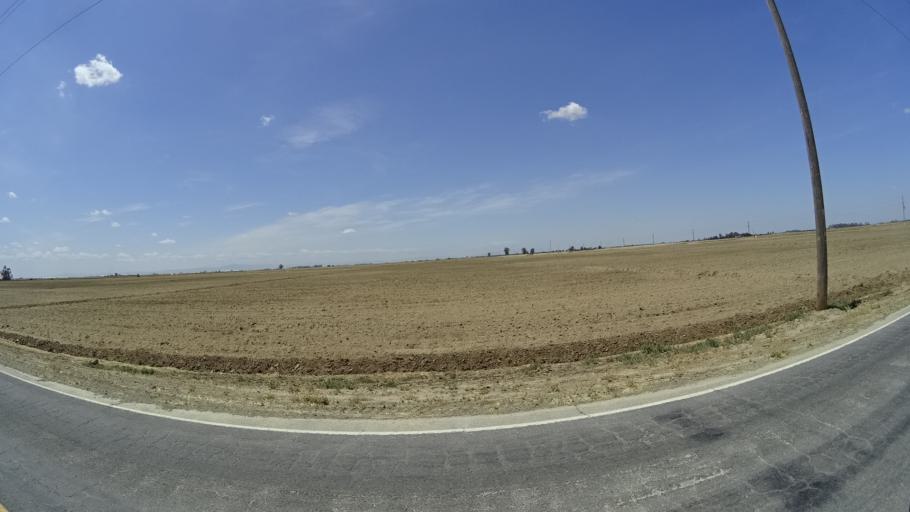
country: US
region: California
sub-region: Kings County
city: Home Garden
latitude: 36.2235
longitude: -119.6549
